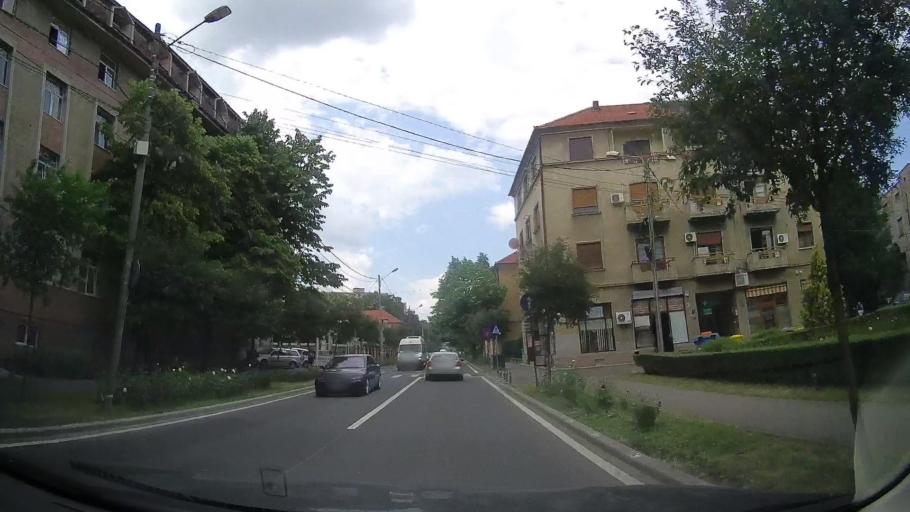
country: RO
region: Timis
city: Timisoara
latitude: 45.7565
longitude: 21.2381
